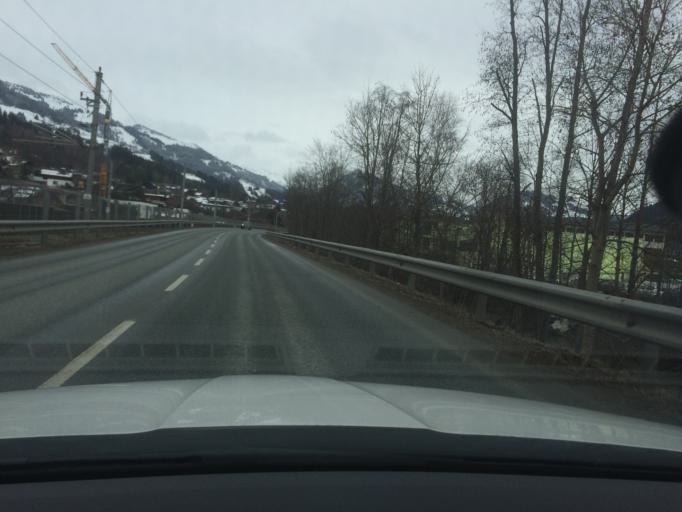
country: AT
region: Tyrol
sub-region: Politischer Bezirk Kitzbuhel
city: Kitzbuhel
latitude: 47.4483
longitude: 12.3942
